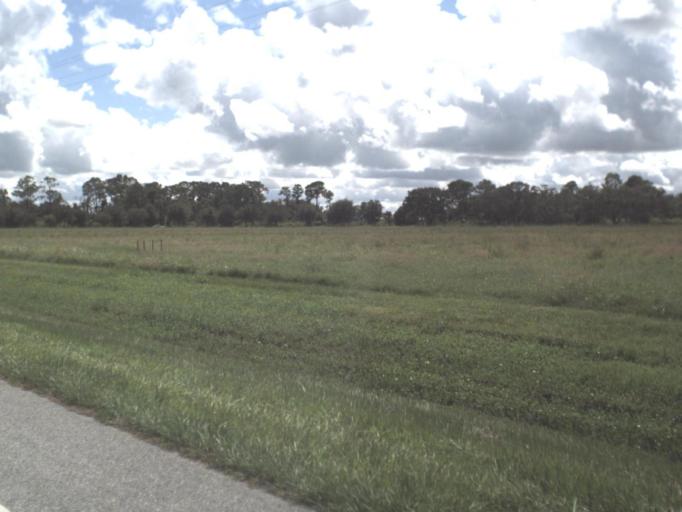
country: US
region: Florida
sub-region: DeSoto County
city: Arcadia
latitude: 27.3267
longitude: -82.1303
